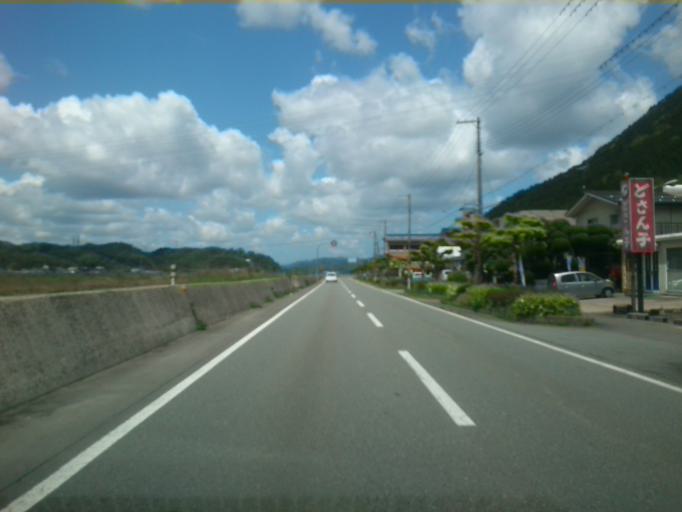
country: JP
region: Hyogo
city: Toyooka
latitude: 35.4492
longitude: 134.8725
